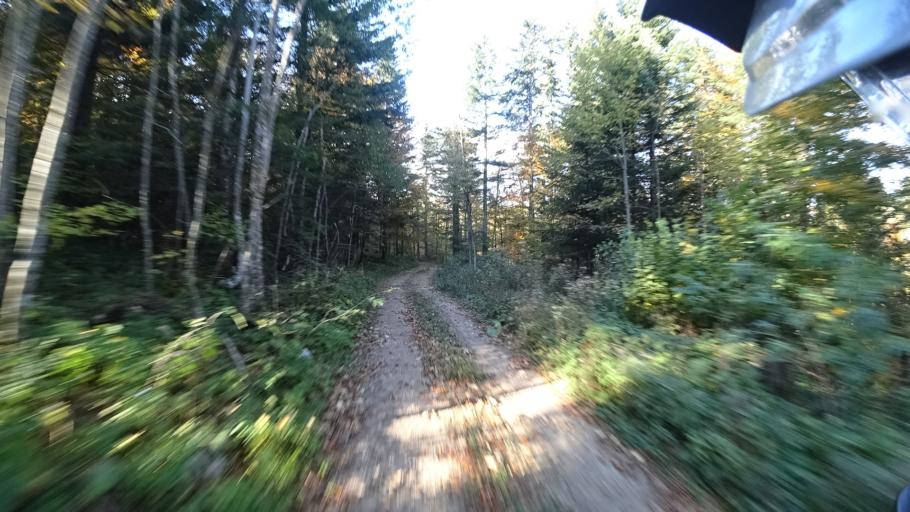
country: HR
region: Karlovacka
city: Plaski
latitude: 45.0193
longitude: 15.3772
